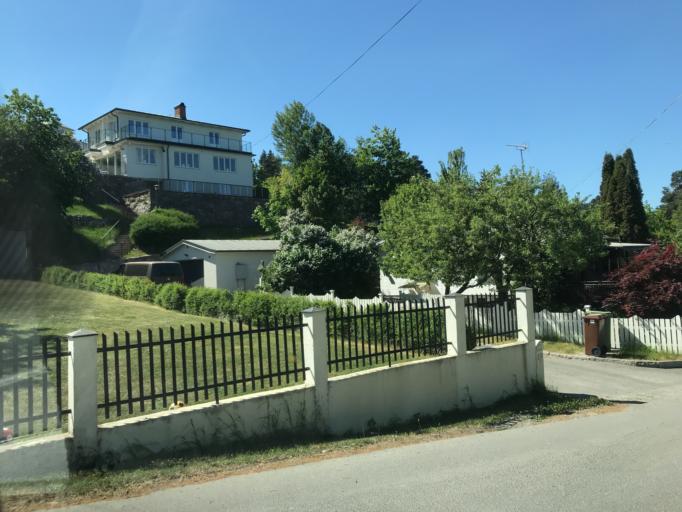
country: SE
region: Stockholm
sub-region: Sollentuna Kommun
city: Sollentuna
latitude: 59.4219
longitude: 17.9780
